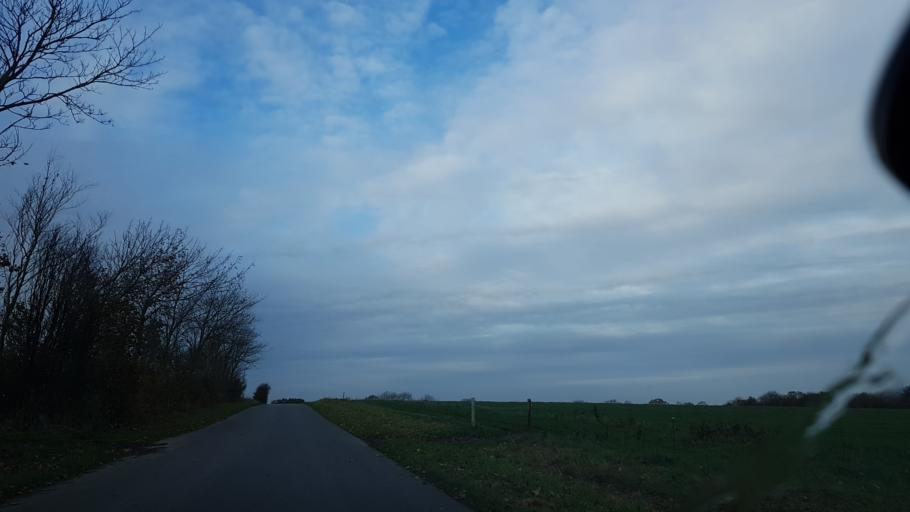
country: DK
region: South Denmark
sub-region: Haderslev Kommune
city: Vojens
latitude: 55.2624
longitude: 9.1888
